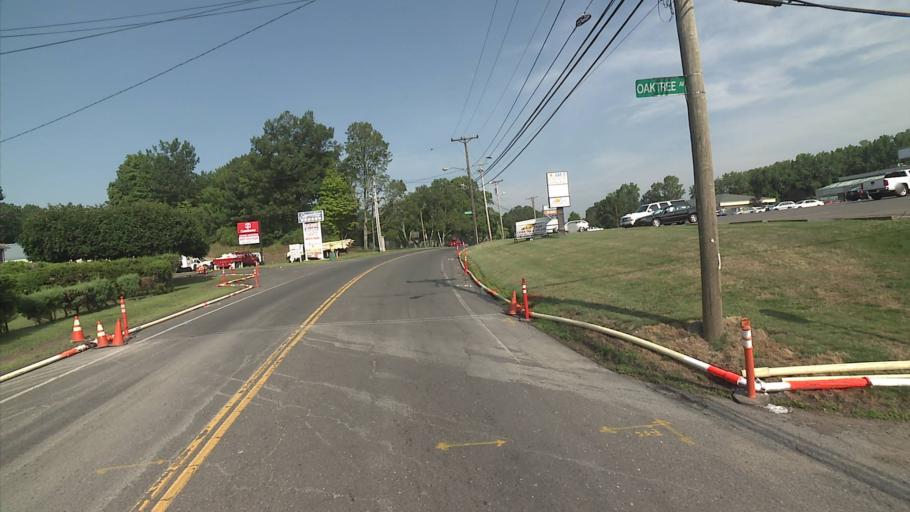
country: US
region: Connecticut
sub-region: New Haven County
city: Prospect
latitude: 41.5419
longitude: -72.9998
